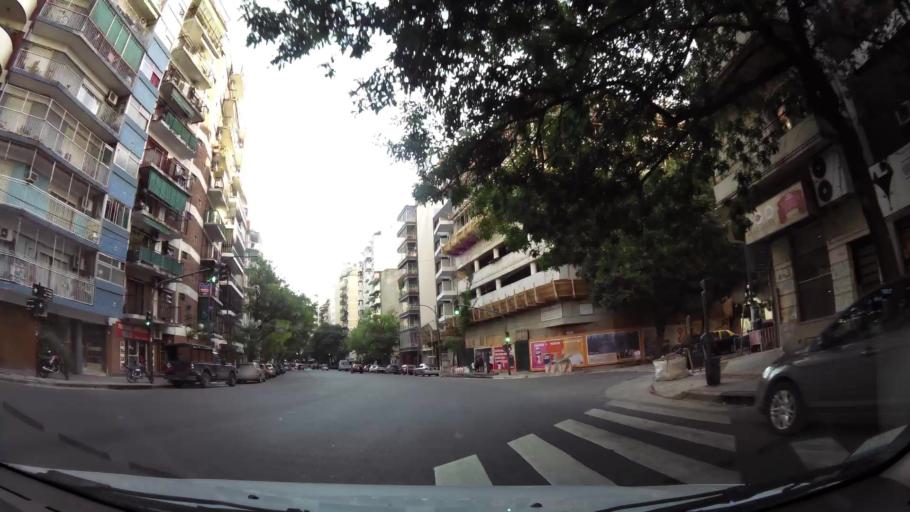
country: AR
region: Buenos Aires F.D.
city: Colegiales
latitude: -34.5990
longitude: -58.4290
